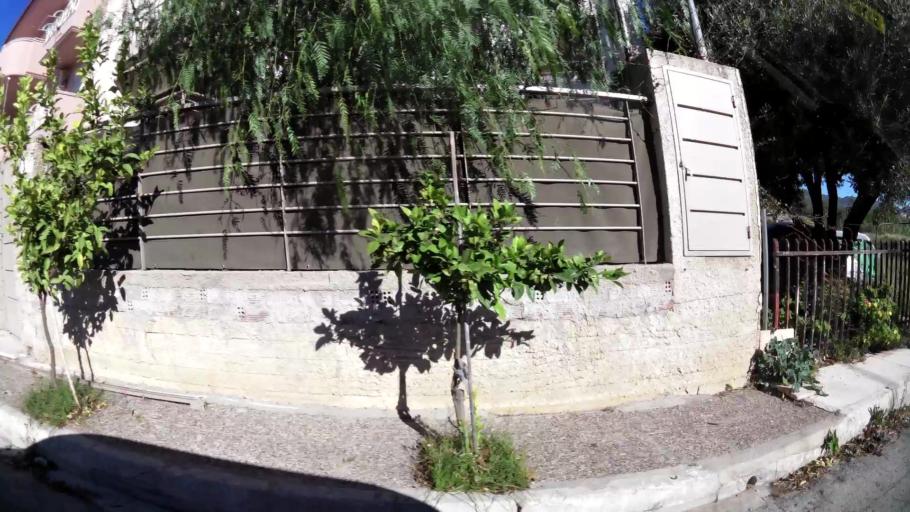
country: GR
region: Attica
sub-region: Nomarchia Anatolikis Attikis
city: Gerakas
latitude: 38.0206
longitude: 23.8494
